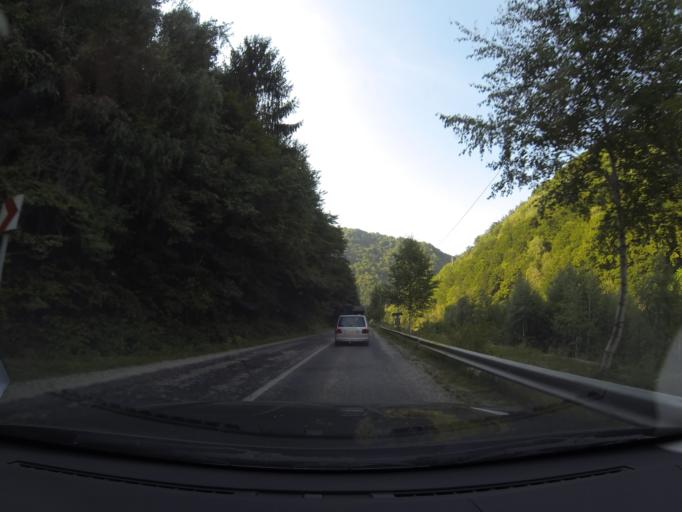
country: RO
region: Arges
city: Poenari
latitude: 45.3452
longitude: 24.6340
